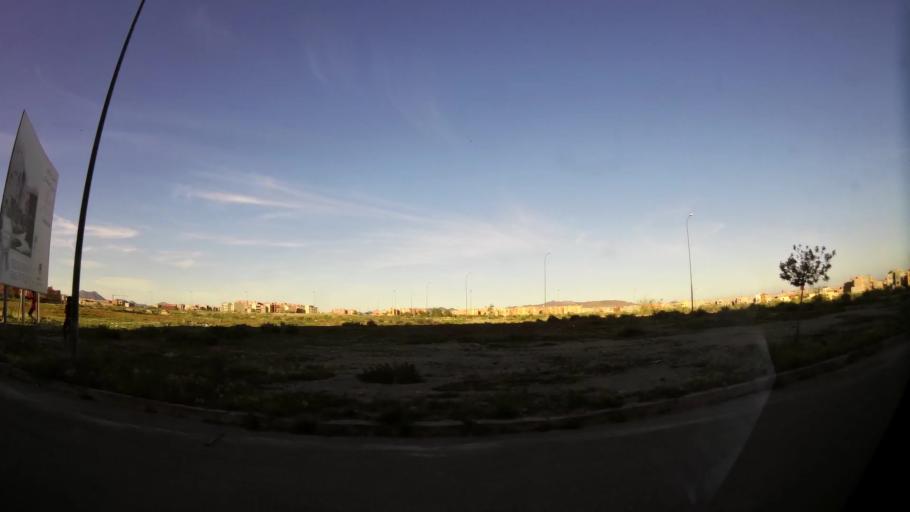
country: MA
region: Marrakech-Tensift-Al Haouz
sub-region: Marrakech
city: Marrakesh
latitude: 31.7472
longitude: -8.1284
